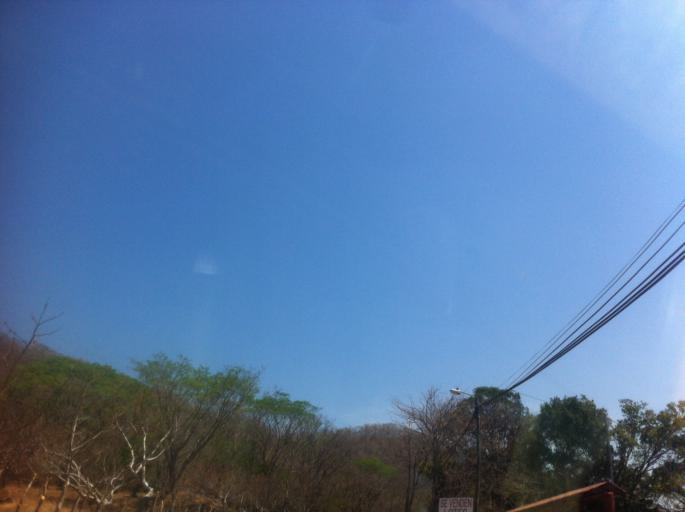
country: CR
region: Guanacaste
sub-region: Canton de Nicoya
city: Nicoya
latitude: 10.1213
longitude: -85.4467
